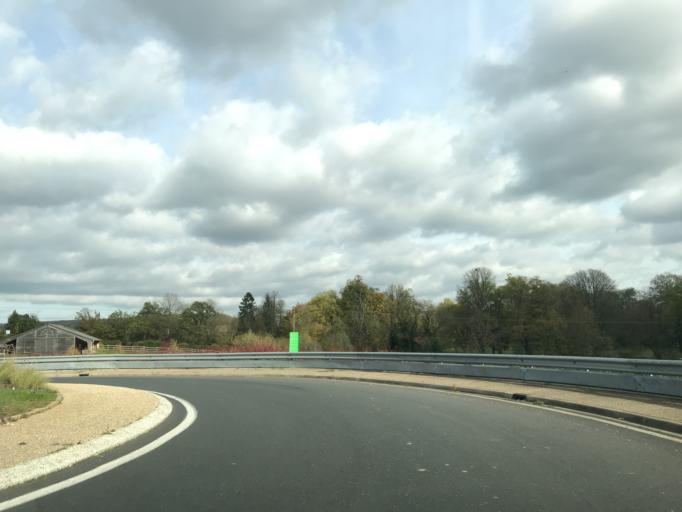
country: FR
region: Haute-Normandie
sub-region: Departement de l'Eure
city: Charleval
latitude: 49.3705
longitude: 1.3706
